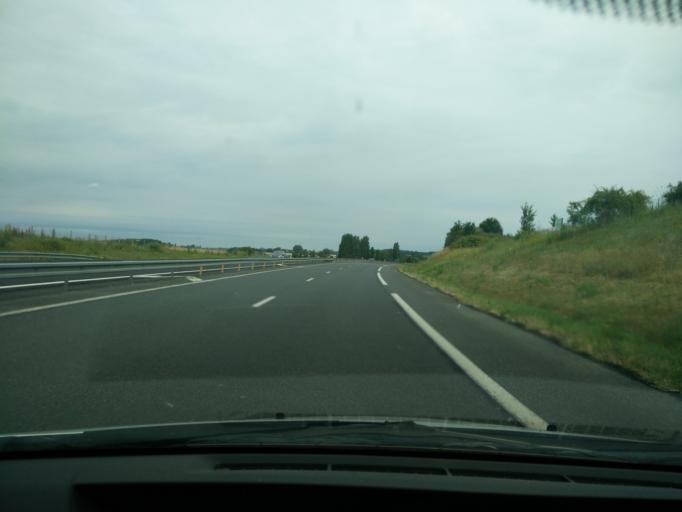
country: FR
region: Pays de la Loire
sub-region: Departement de Maine-et-Loire
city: Doue-la-Fontaine
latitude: 47.2371
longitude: -0.3200
